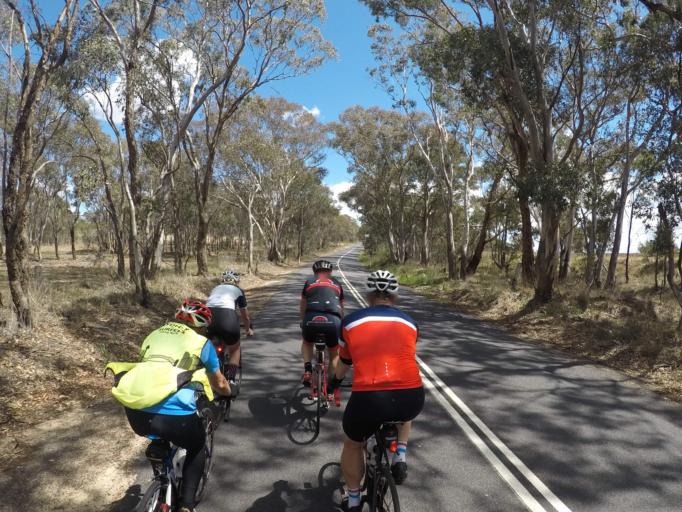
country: AU
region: New South Wales
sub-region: Bathurst Regional
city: Perthville
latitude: -33.5307
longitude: 149.4544
